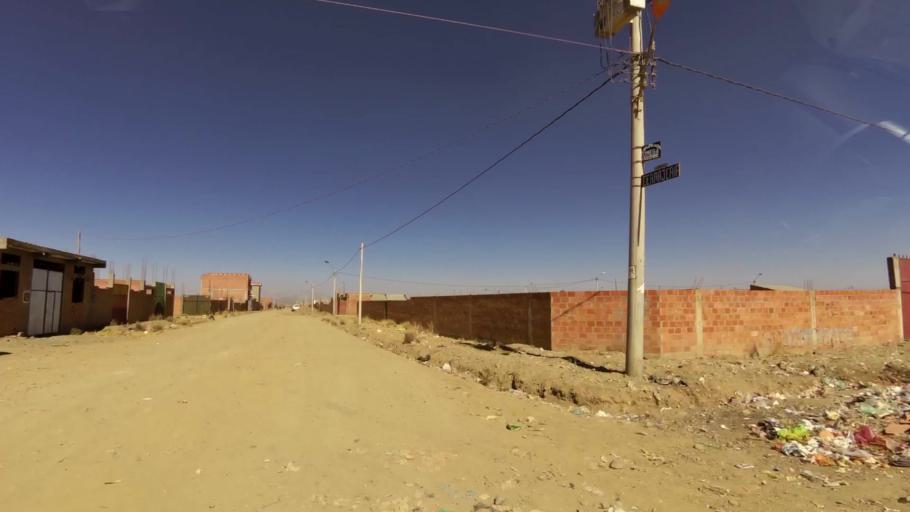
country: BO
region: La Paz
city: La Paz
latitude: -16.5888
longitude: -68.2037
